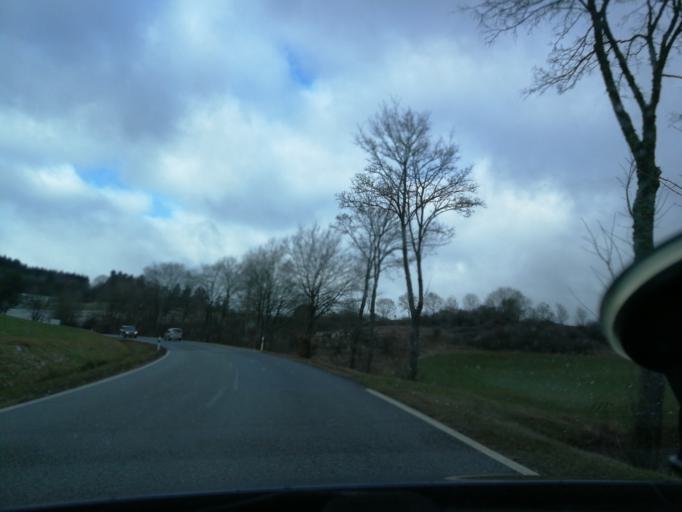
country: DE
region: Rheinland-Pfalz
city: Oberehe-Stroheich
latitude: 50.2784
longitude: 6.7601
